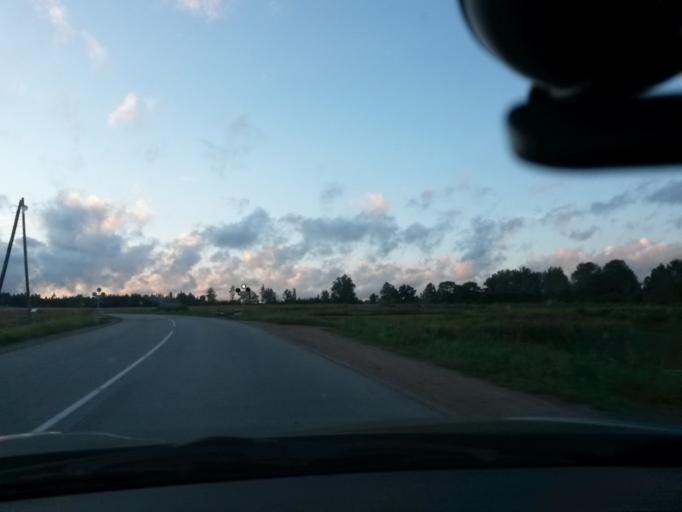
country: LV
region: Jekabpils Rajons
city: Jekabpils
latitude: 56.6890
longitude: 25.9868
